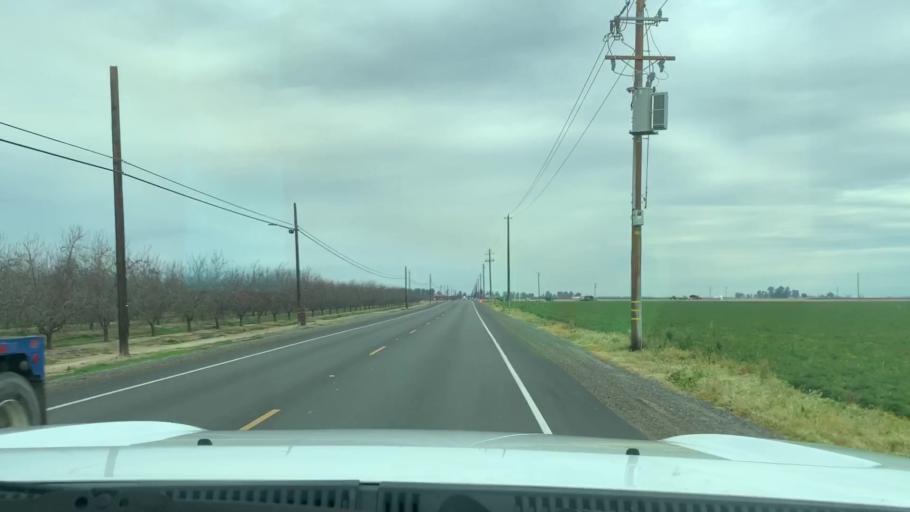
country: US
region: California
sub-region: Kern County
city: Shafter
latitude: 35.4066
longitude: -119.2519
